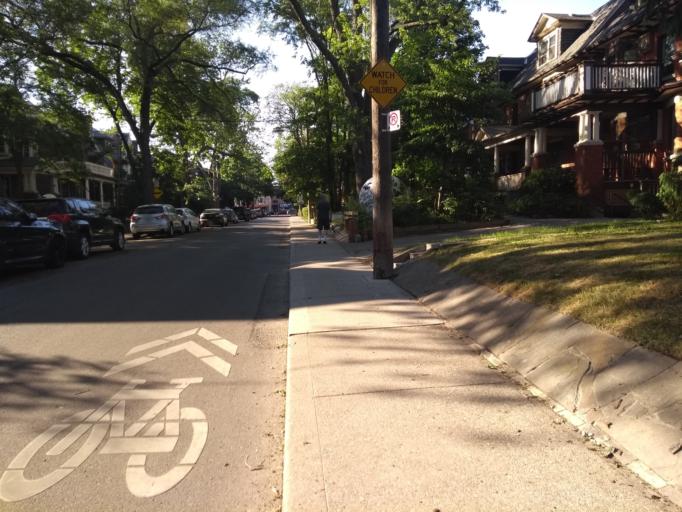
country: CA
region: Ontario
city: Toronto
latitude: 43.6381
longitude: -79.4405
